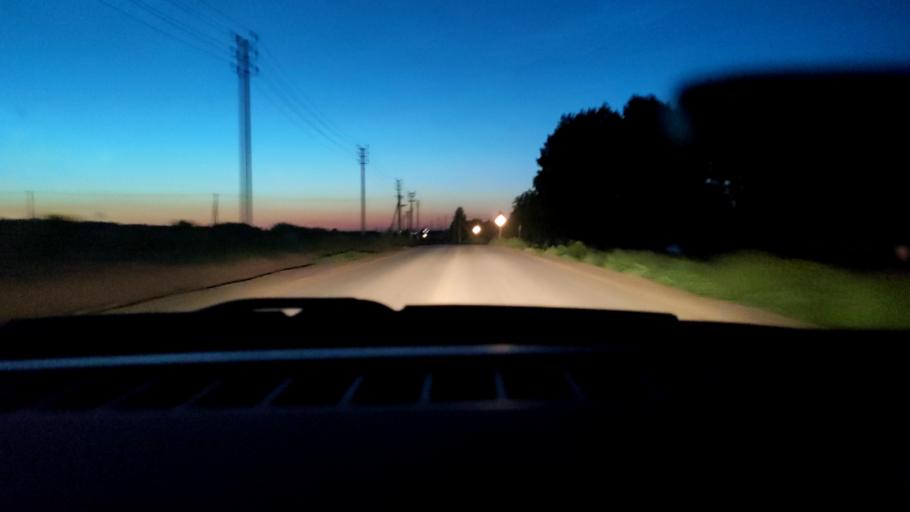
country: RU
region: Perm
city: Kultayevo
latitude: 57.8720
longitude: 55.9861
